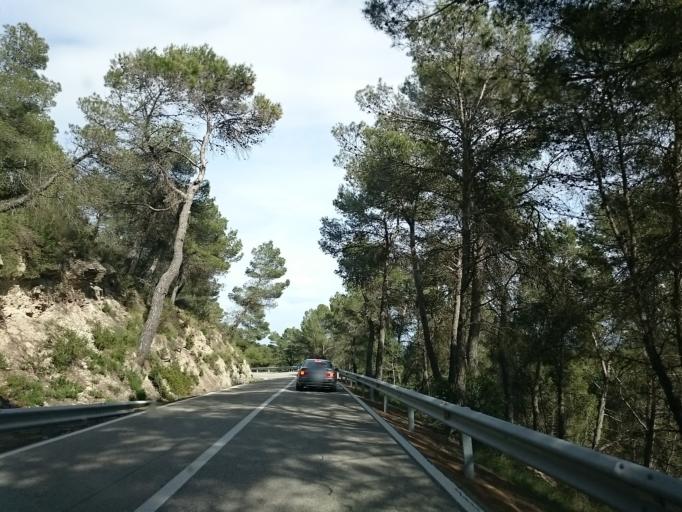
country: ES
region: Catalonia
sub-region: Provincia de Barcelona
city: Sant Marti de Tous
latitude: 41.5700
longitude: 1.4842
